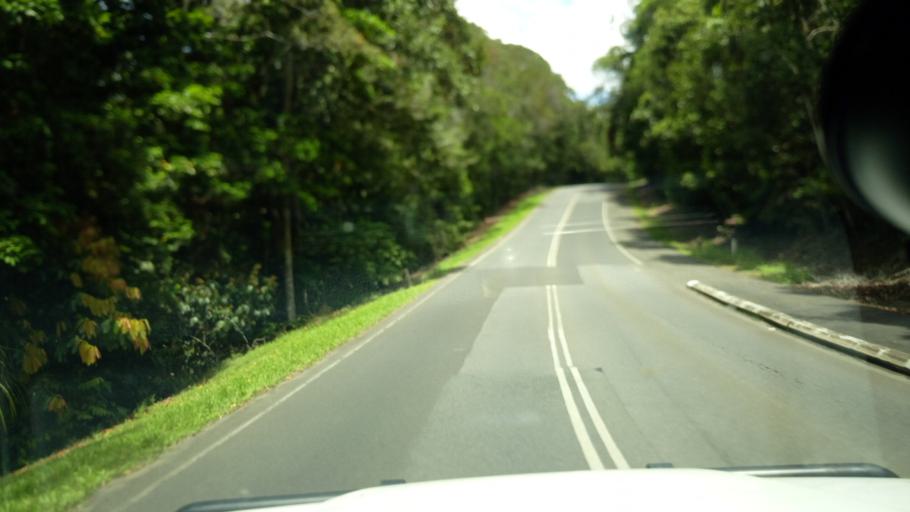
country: AU
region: Queensland
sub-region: Tablelands
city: Kuranda
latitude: -16.8125
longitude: 145.6200
